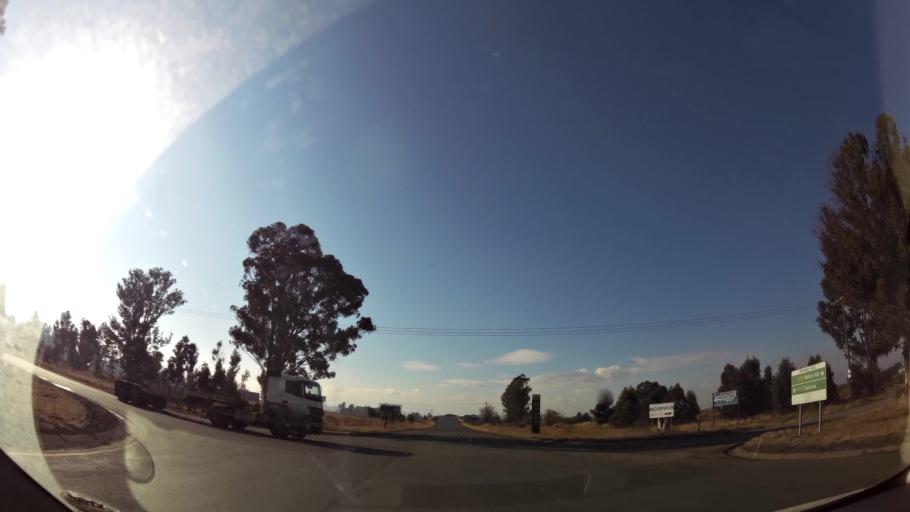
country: ZA
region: Gauteng
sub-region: Sedibeng District Municipality
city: Meyerton
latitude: -26.4904
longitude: 28.0563
